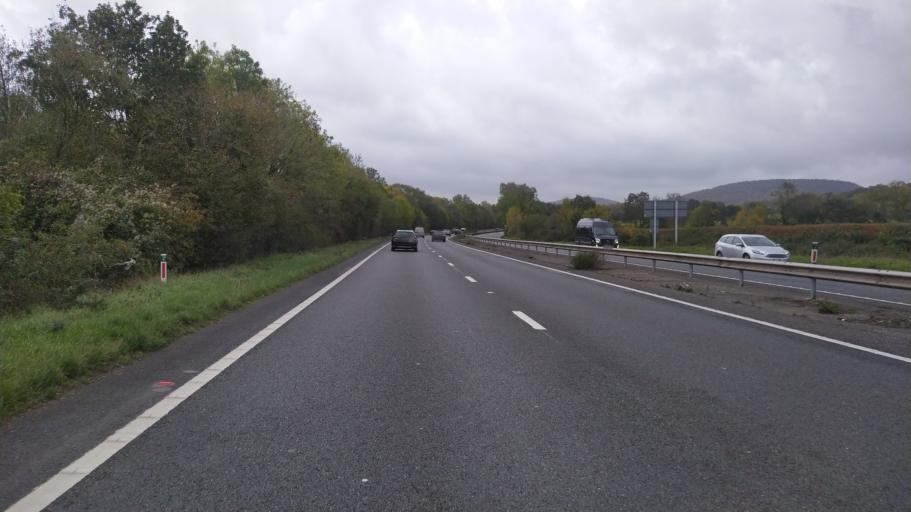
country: GB
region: England
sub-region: Hampshire
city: Petersfield
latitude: 51.0025
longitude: -0.9514
